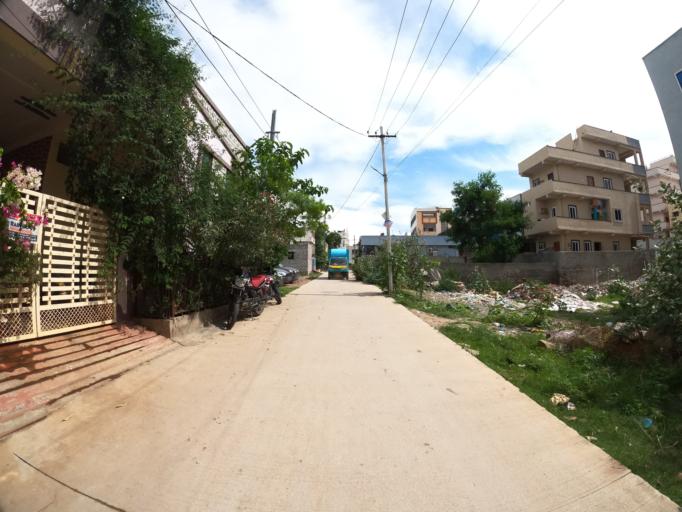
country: IN
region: Telangana
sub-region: Hyderabad
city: Hyderabad
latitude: 17.3668
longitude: 78.3869
